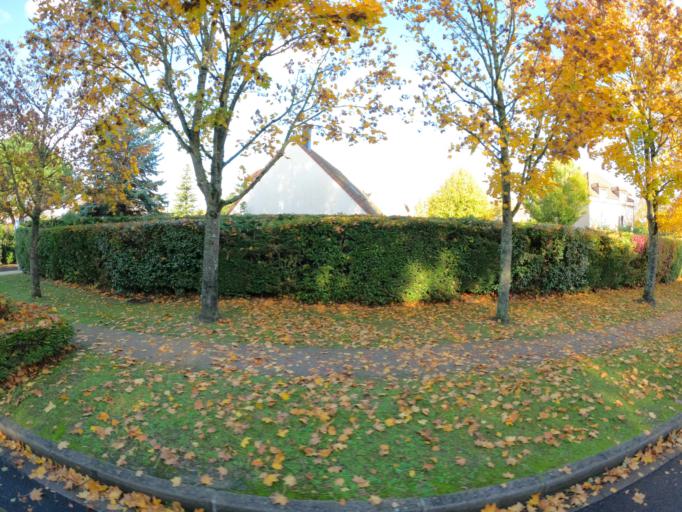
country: FR
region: Ile-de-France
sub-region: Departement de Seine-et-Marne
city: Bailly-Romainvilliers
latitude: 48.8483
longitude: 2.8289
